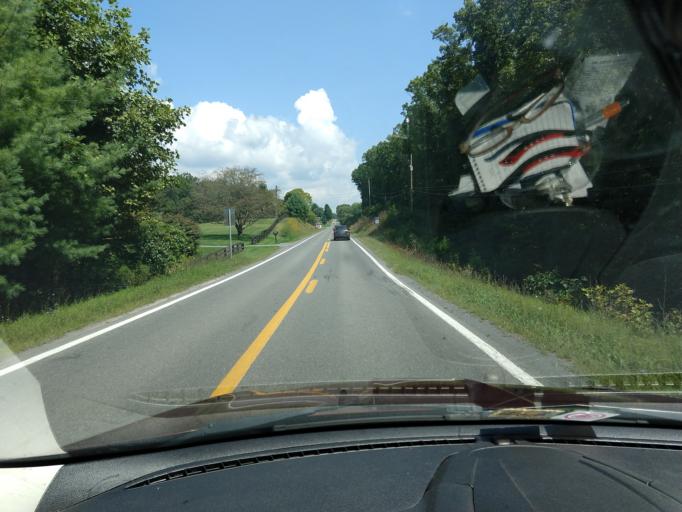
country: US
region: West Virginia
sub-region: Greenbrier County
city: Fairlea
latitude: 37.8424
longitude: -80.5528
